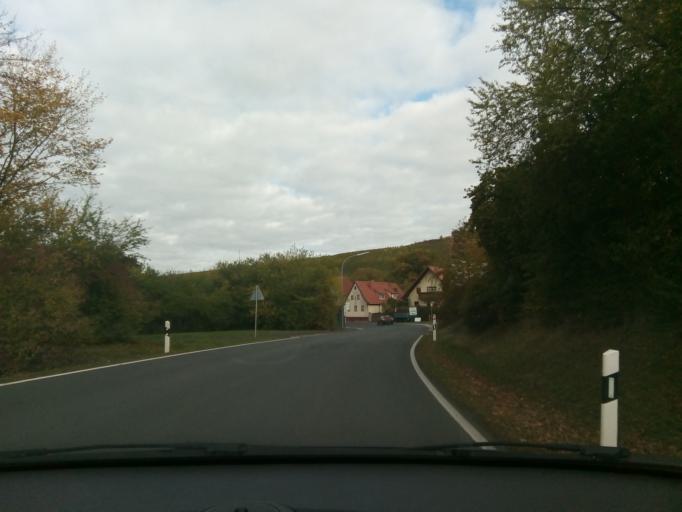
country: DE
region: Bavaria
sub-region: Regierungsbezirk Unterfranken
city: Dingolshausen
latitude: 49.8782
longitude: 10.3897
